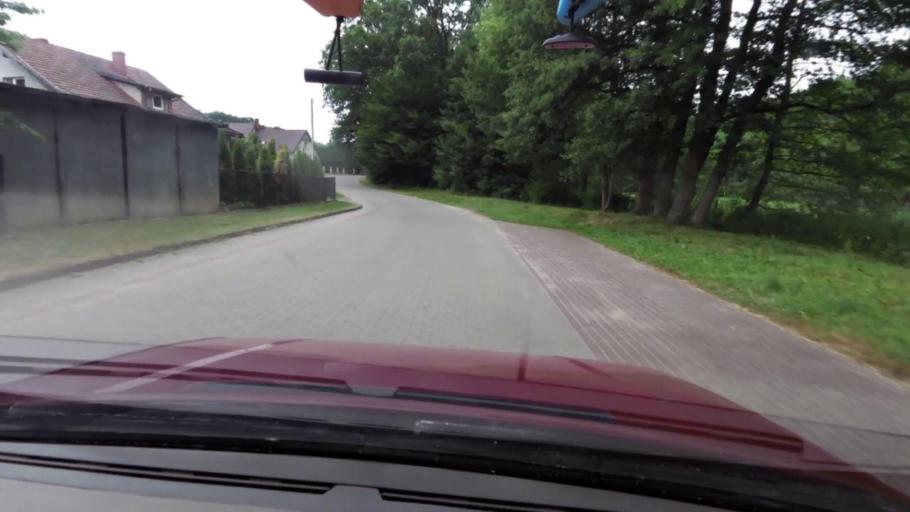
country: PL
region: Pomeranian Voivodeship
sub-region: Powiat slupski
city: Kepice
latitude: 54.2435
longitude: 16.8949
